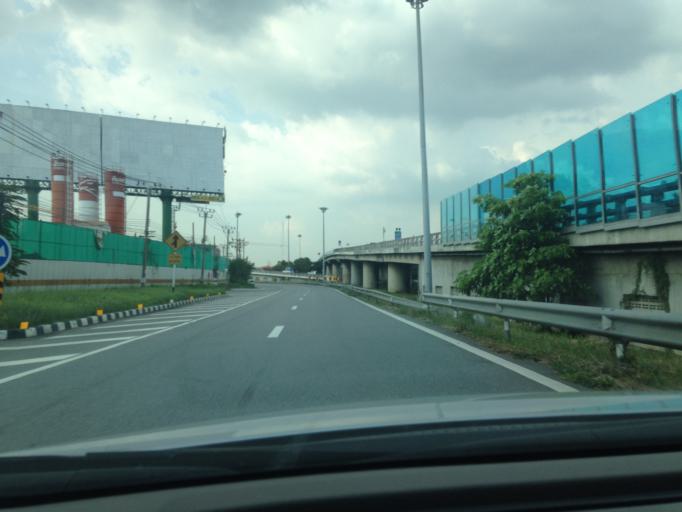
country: TH
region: Bangkok
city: Khan Na Yao
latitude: 13.8250
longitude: 100.6740
